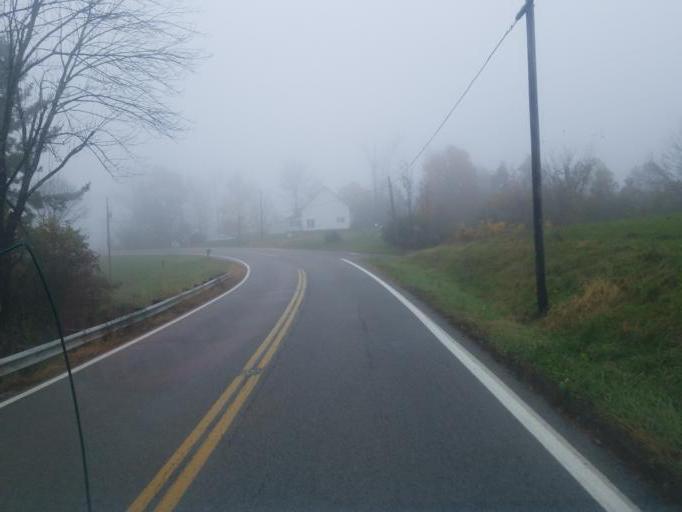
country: US
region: Ohio
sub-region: Morgan County
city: McConnelsville
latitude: 39.6097
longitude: -81.8736
